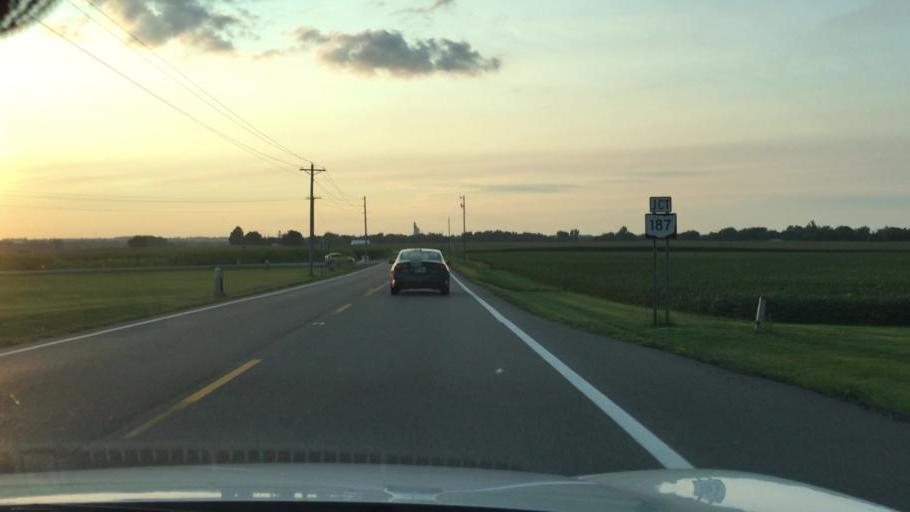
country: US
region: Ohio
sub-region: Champaign County
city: Mechanicsburg
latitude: 40.0576
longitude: -83.5337
